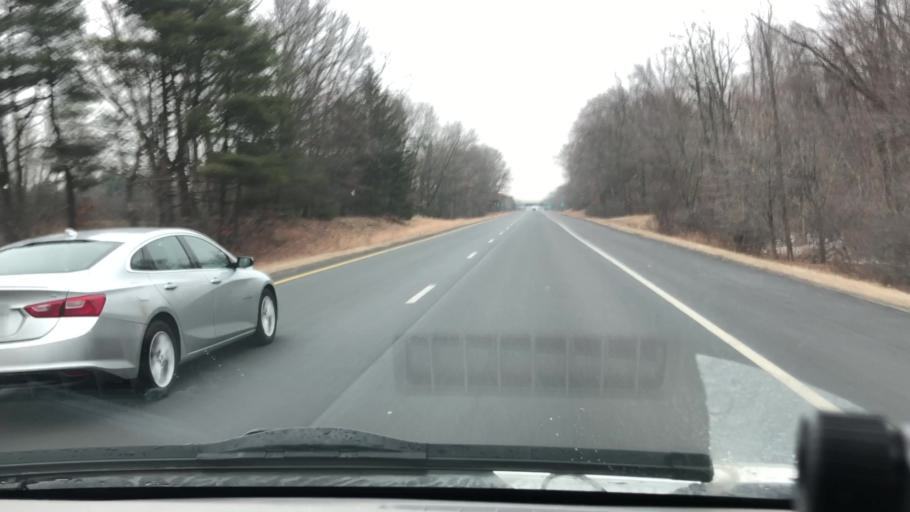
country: US
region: Massachusetts
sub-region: Franklin County
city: Whately
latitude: 42.4041
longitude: -72.6276
